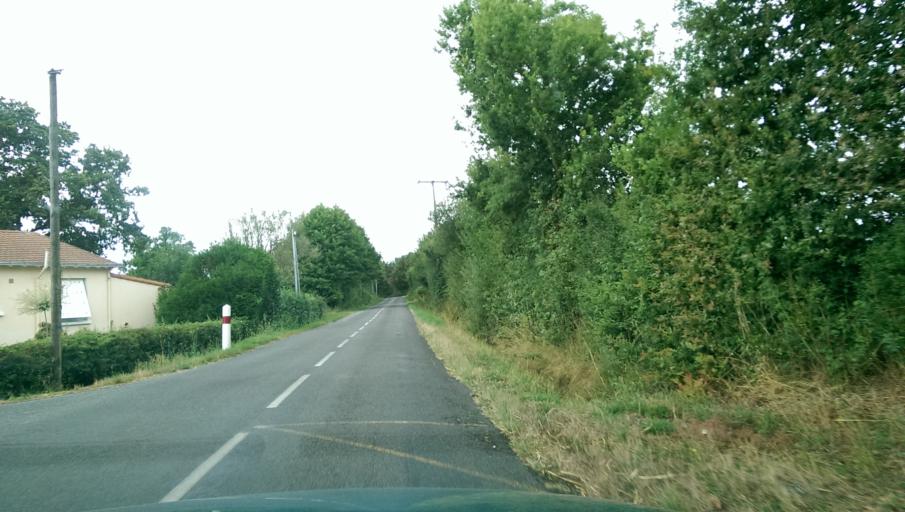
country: FR
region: Pays de la Loire
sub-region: Departement de la Loire-Atlantique
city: La Planche
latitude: 47.0032
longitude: -1.4052
